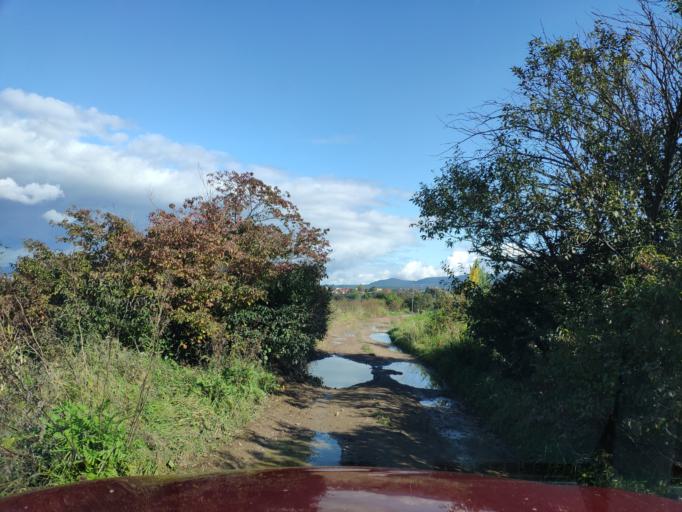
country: SK
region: Presovsky
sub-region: Okres Presov
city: Presov
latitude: 48.9408
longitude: 21.2822
